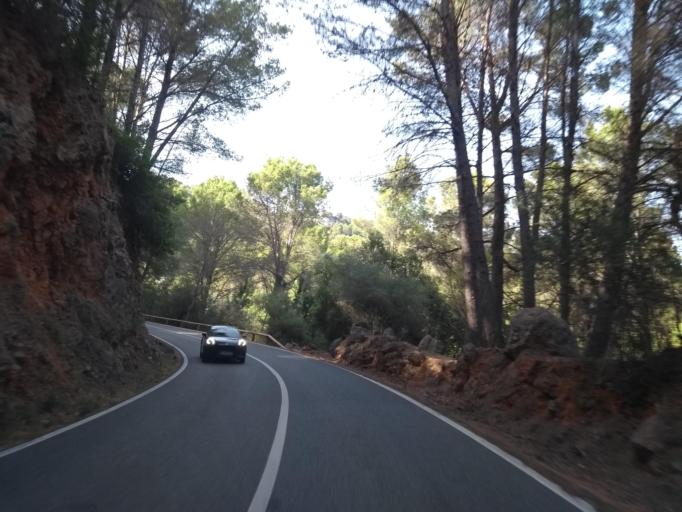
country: ES
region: Balearic Islands
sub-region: Illes Balears
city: Fornalutx
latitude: 39.7817
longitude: 2.7310
